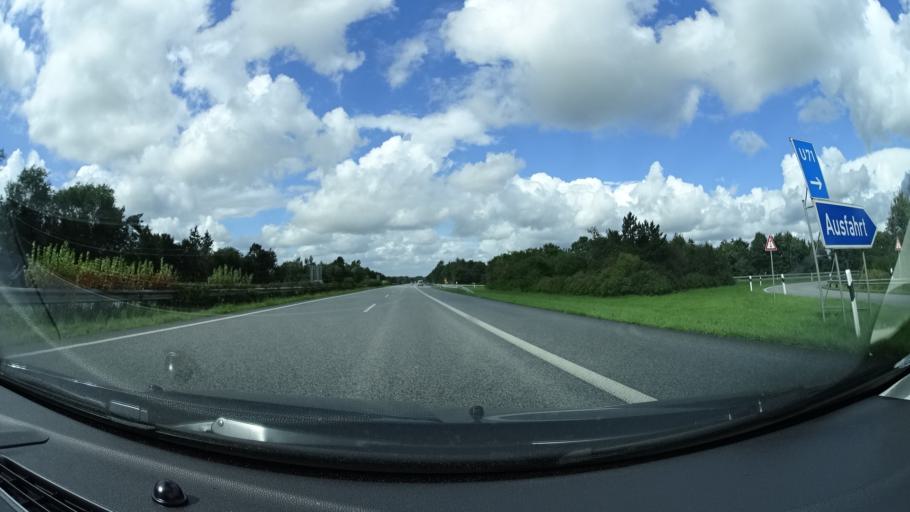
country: DE
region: Schleswig-Holstein
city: Handewitt
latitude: 54.7731
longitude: 9.3462
